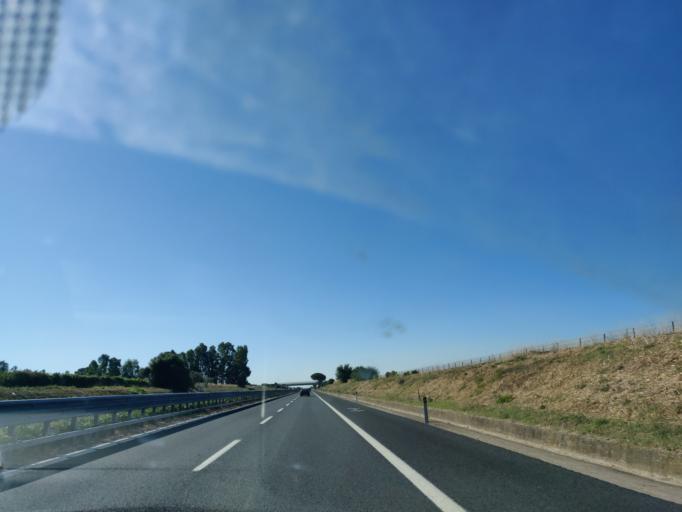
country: IT
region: Latium
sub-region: Citta metropolitana di Roma Capitale
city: Marina San Nicola
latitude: 41.9581
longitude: 12.1259
